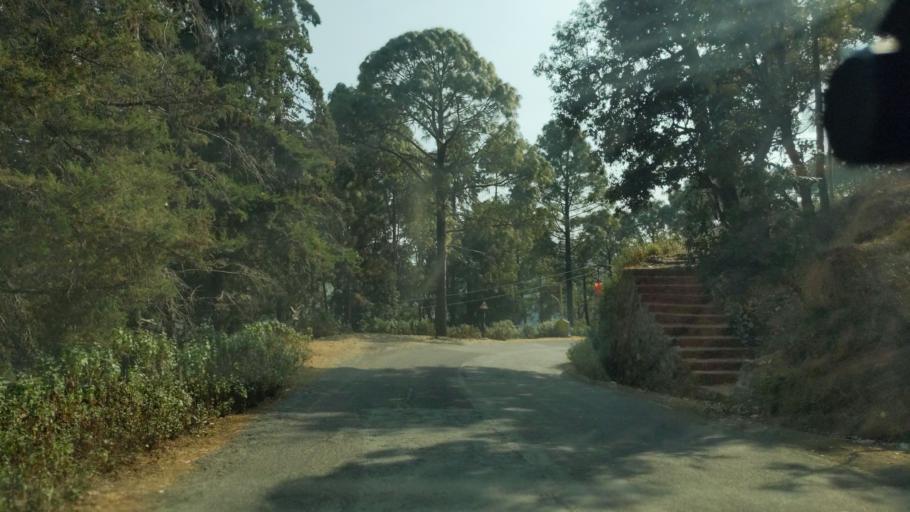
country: IN
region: Uttarakhand
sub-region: Naini Tal
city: Bhowali
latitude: 29.3895
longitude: 79.5402
